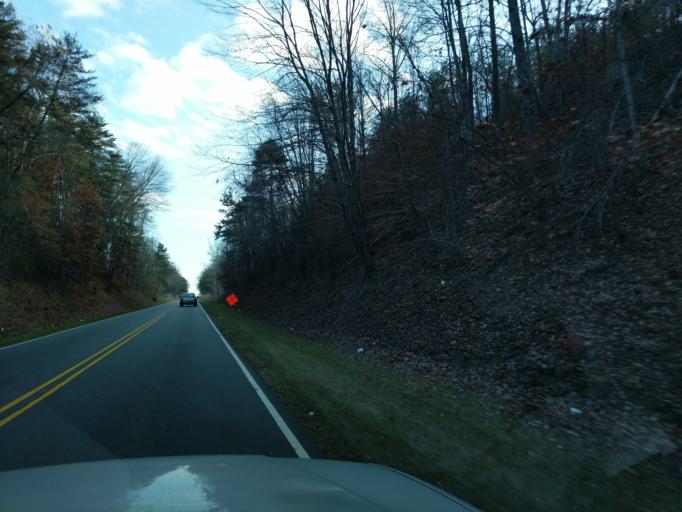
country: US
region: North Carolina
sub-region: Rutherford County
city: Rutherfordton
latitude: 35.4161
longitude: -81.9743
